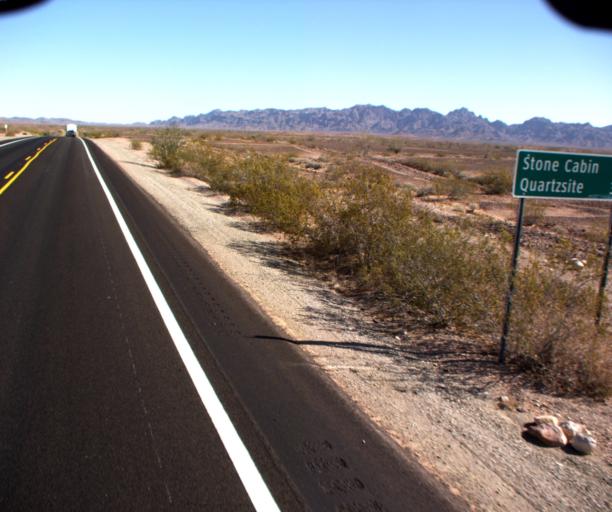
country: US
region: Arizona
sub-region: Yuma County
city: Wellton
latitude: 33.1169
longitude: -114.2933
